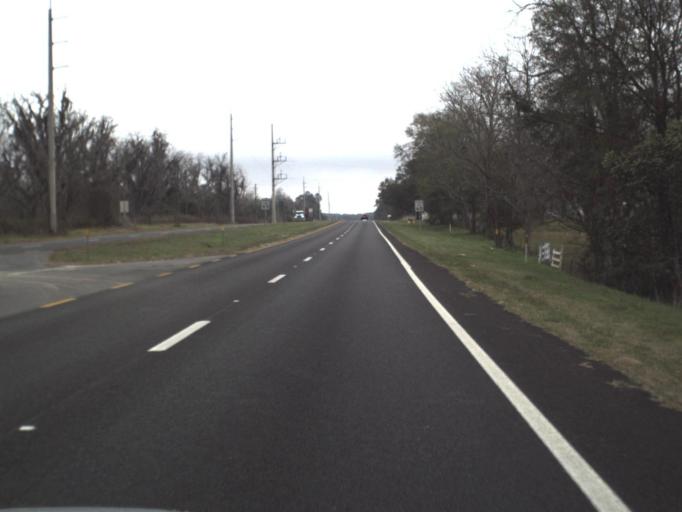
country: US
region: Florida
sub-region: Jefferson County
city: Monticello
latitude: 30.4118
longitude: -83.9413
